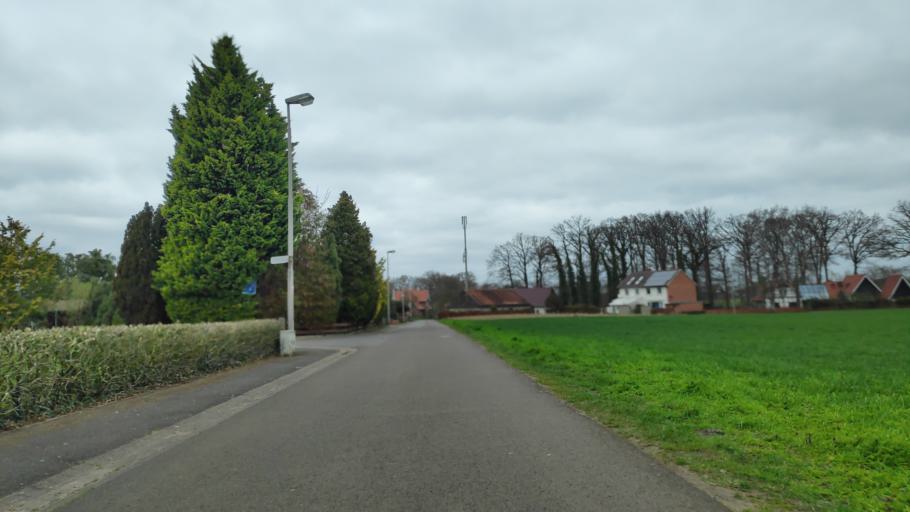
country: DE
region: North Rhine-Westphalia
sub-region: Regierungsbezirk Detmold
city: Minden
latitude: 52.3547
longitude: 8.8613
